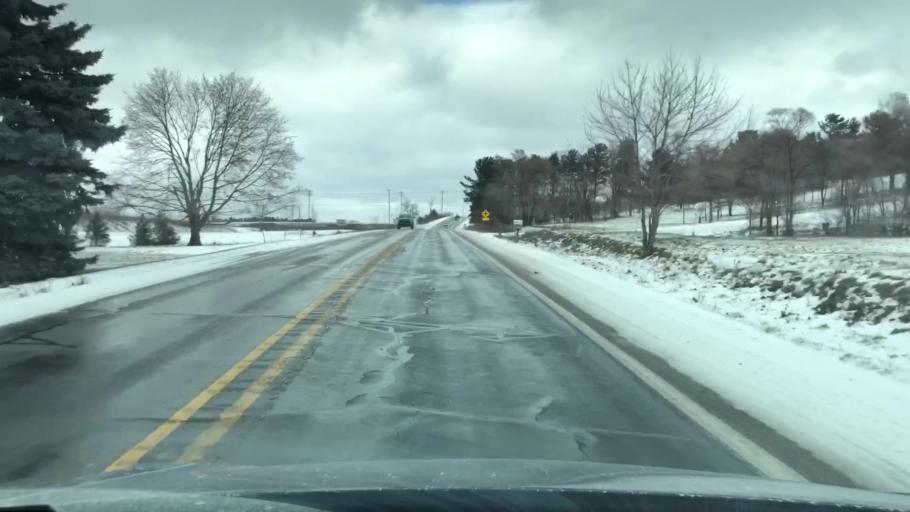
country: US
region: Michigan
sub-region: Antrim County
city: Elk Rapids
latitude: 44.8595
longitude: -85.5227
